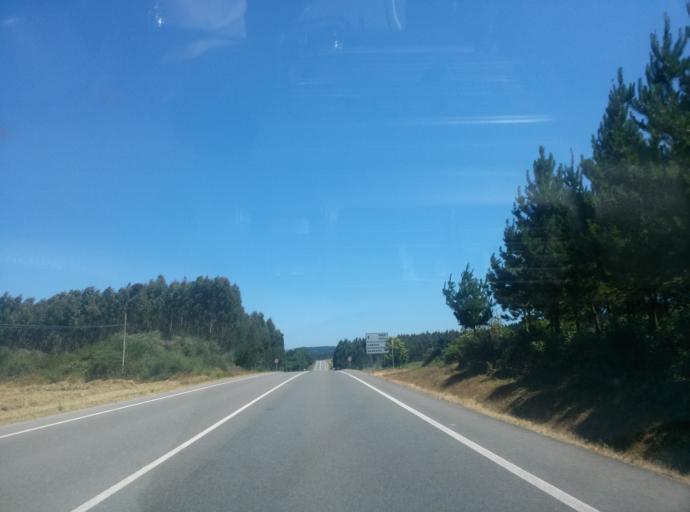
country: ES
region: Galicia
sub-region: Provincia de Lugo
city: Castro de Rei
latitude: 43.2374
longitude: -7.4069
